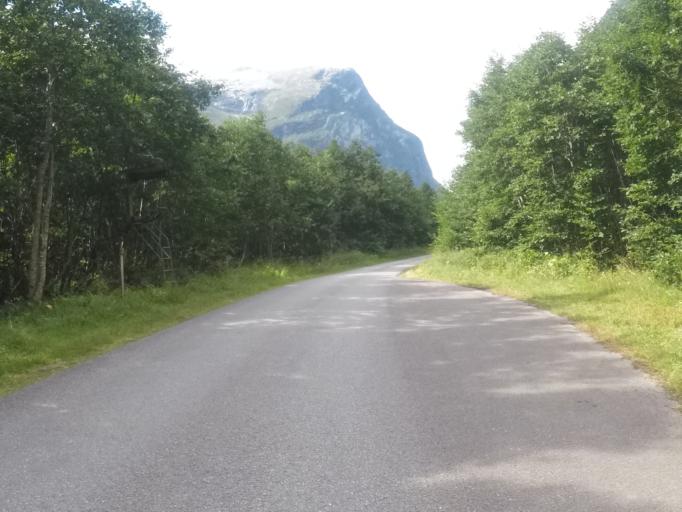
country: NO
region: Sogn og Fjordane
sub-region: Stryn
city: Stryn
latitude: 61.7733
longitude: 7.0241
